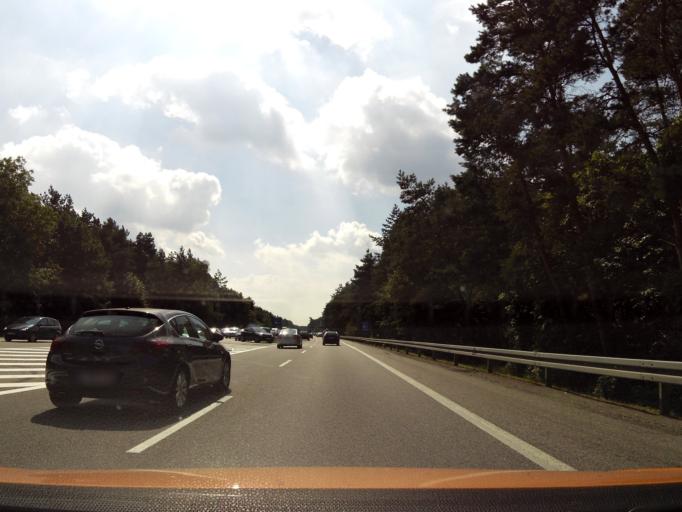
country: PL
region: West Pomeranian Voivodeship
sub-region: Powiat goleniowski
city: Goleniow
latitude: 53.4683
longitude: 14.7873
